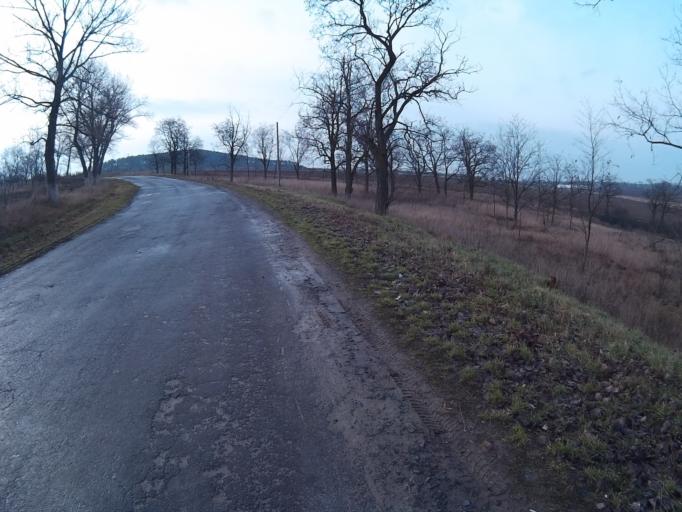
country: HU
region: Borsod-Abauj-Zemplen
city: Abaujszanto
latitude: 48.3438
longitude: 21.2147
